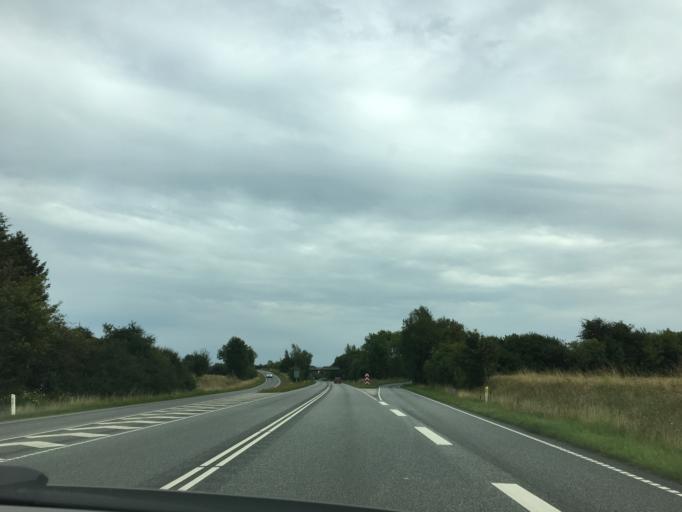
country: DK
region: South Denmark
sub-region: Vejle Kommune
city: Brejning
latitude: 55.6349
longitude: 9.6825
